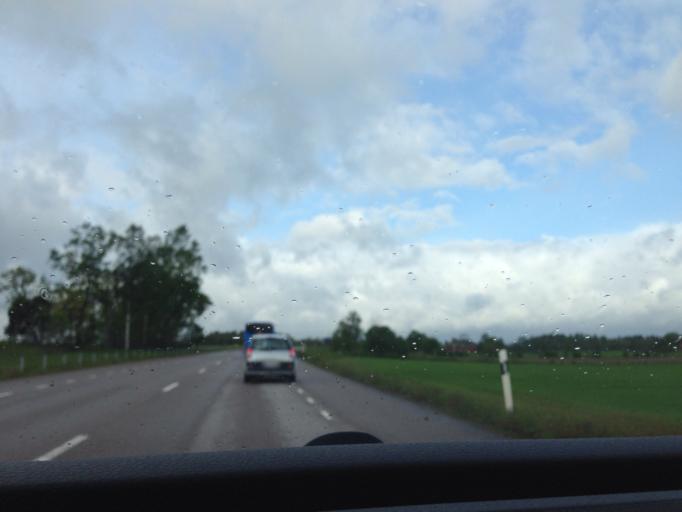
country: SE
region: Vaestra Goetaland
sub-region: Tibro Kommun
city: Tibro
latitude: 58.4099
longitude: 14.0324
